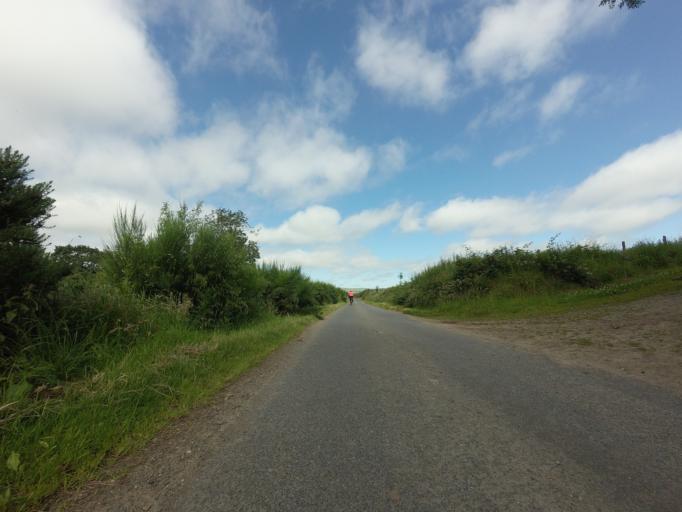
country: GB
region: Scotland
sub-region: Aberdeenshire
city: Turriff
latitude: 57.5702
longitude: -2.4986
